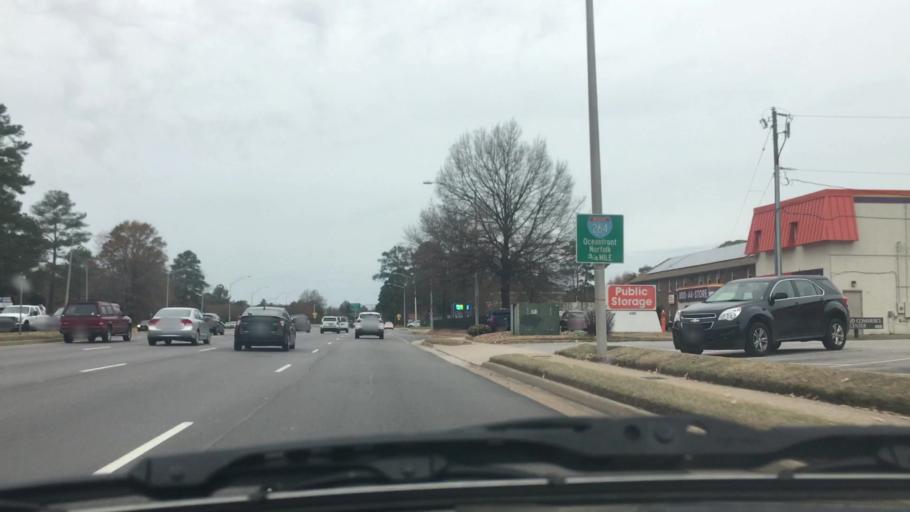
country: US
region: Virginia
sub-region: City of Chesapeake
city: Chesapeake
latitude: 36.8275
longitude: -76.1327
